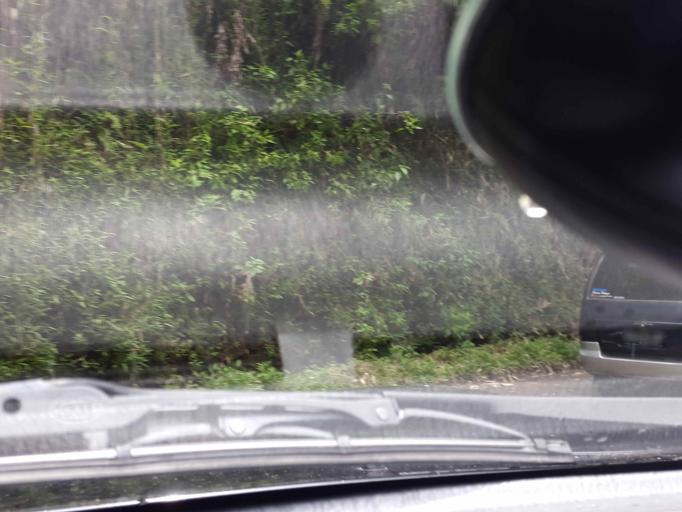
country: ID
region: Central Java
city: Wonosobo
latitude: -7.3607
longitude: 110.0188
